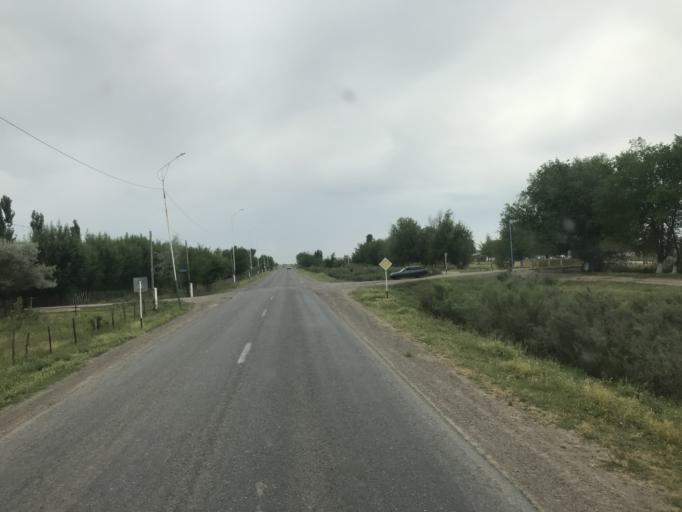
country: KZ
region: Ongtustik Qazaqstan
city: Asykata
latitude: 40.9287
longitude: 68.4055
